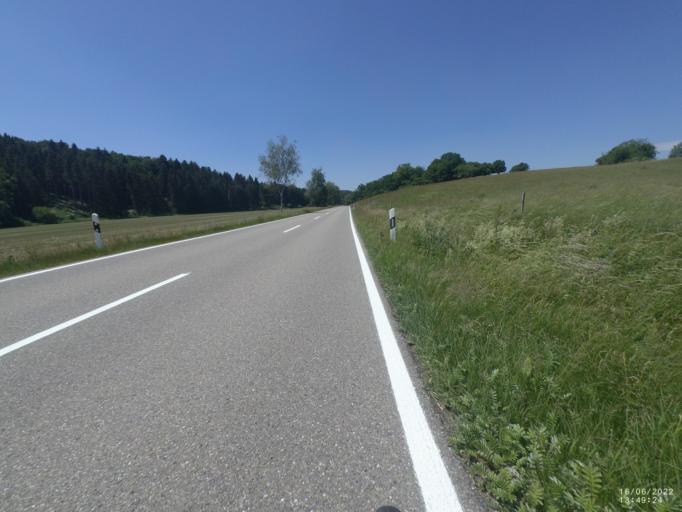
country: DE
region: Baden-Wuerttemberg
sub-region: Tuebingen Region
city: Ballendorf
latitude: 48.5847
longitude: 10.0753
